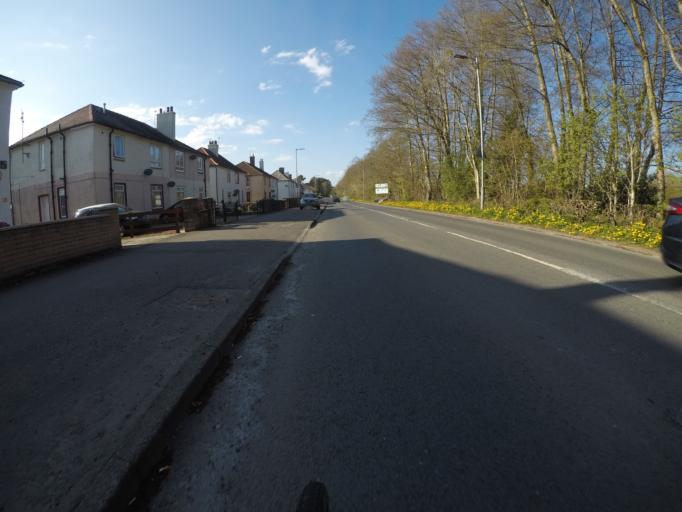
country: GB
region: Scotland
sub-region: North Ayrshire
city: Kilwinning
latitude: 55.6470
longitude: -4.6872
